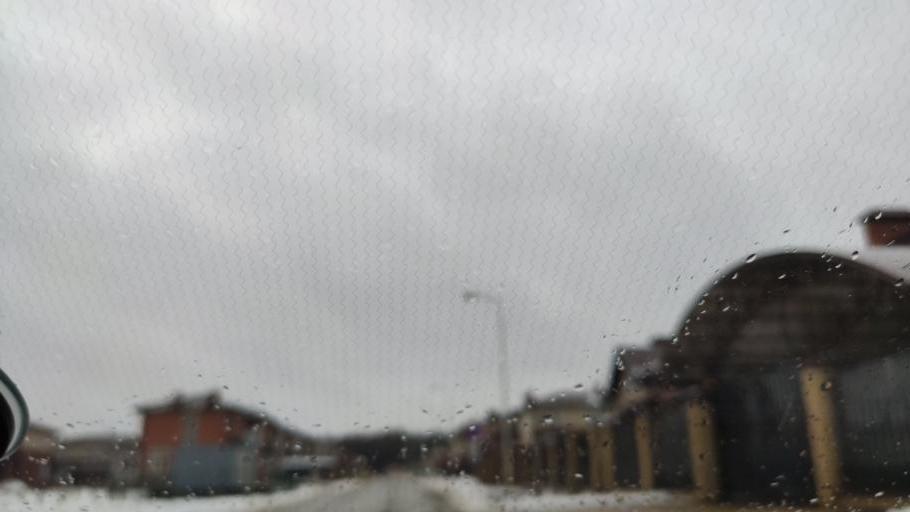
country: RU
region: Moskovskaya
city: Vatutinki
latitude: 55.4288
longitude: 37.3829
